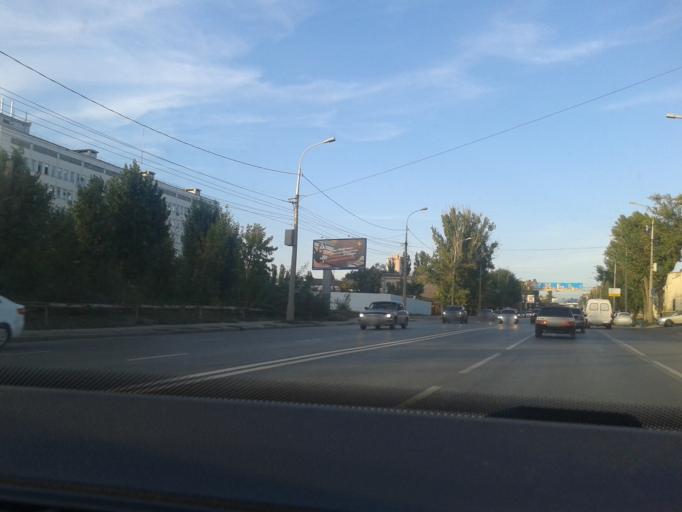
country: RU
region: Volgograd
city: Volgograd
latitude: 48.7117
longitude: 44.4944
